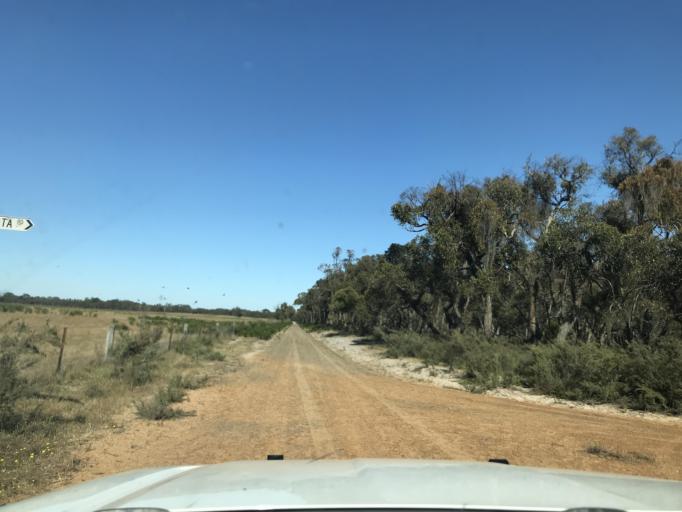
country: AU
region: South Australia
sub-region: Wattle Range
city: Penola
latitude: -37.0818
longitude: 141.3965
